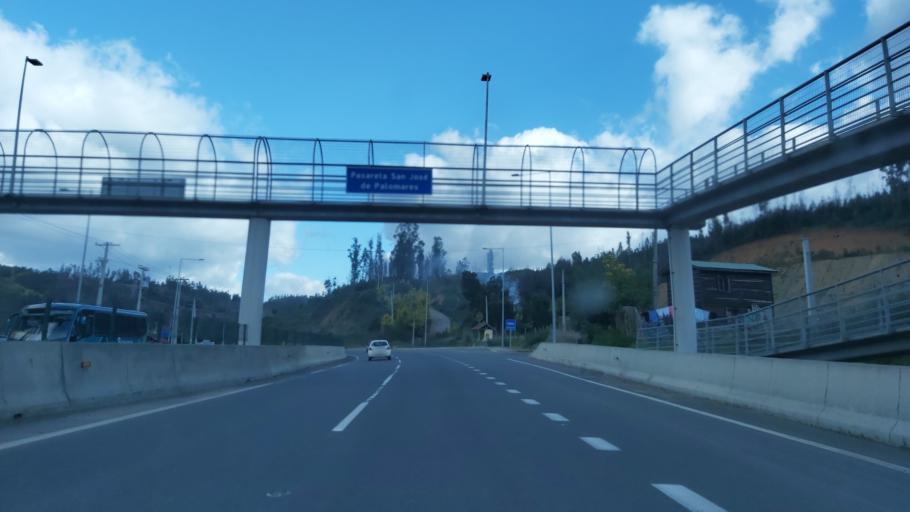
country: CL
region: Biobio
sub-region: Provincia de Concepcion
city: Penco
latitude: -36.8208
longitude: -72.9319
